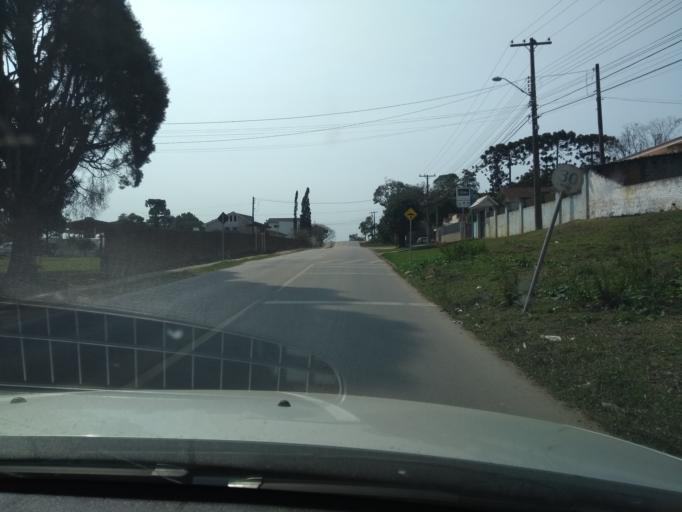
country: BR
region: Parana
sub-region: Araucaria
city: Araucaria
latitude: -25.6158
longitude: -49.3441
